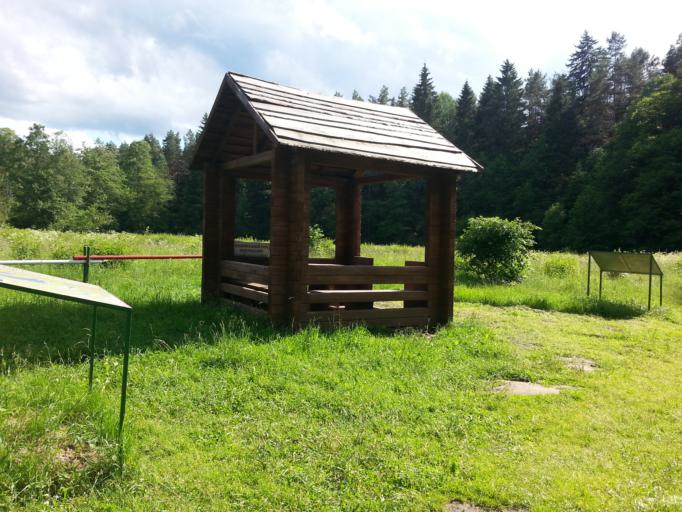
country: BY
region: Vitebsk
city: Lyntupy
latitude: 54.9620
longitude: 26.3650
